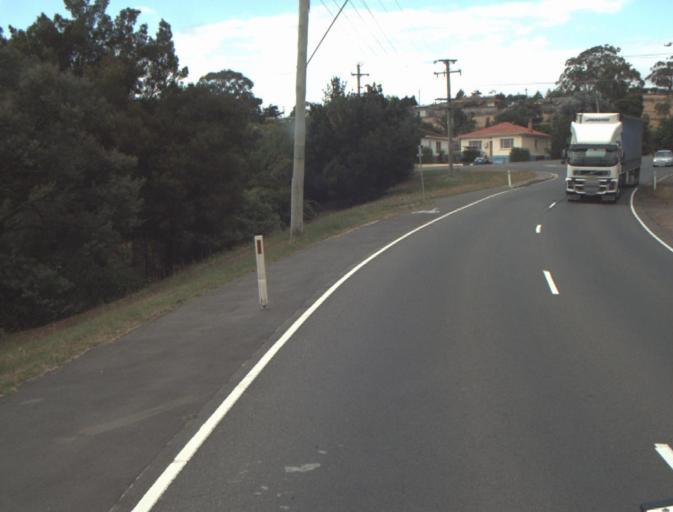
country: AU
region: Tasmania
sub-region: Launceston
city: Newstead
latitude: -41.4557
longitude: 147.1982
